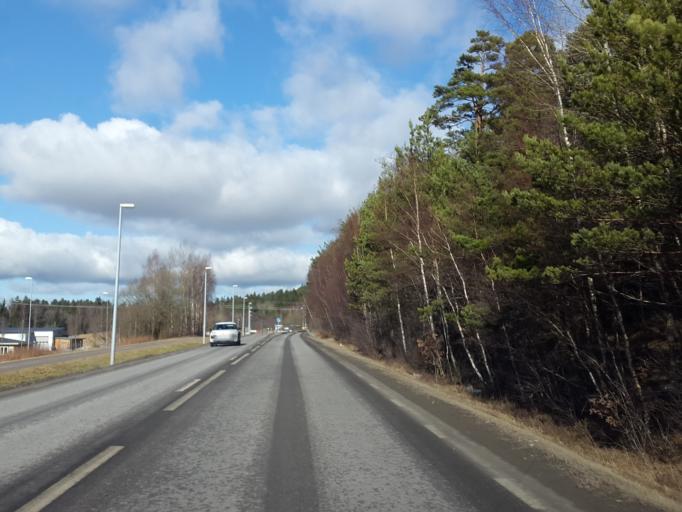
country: SE
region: Vaestra Goetaland
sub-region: Lerums Kommun
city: Stenkullen
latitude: 57.8013
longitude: 12.3071
